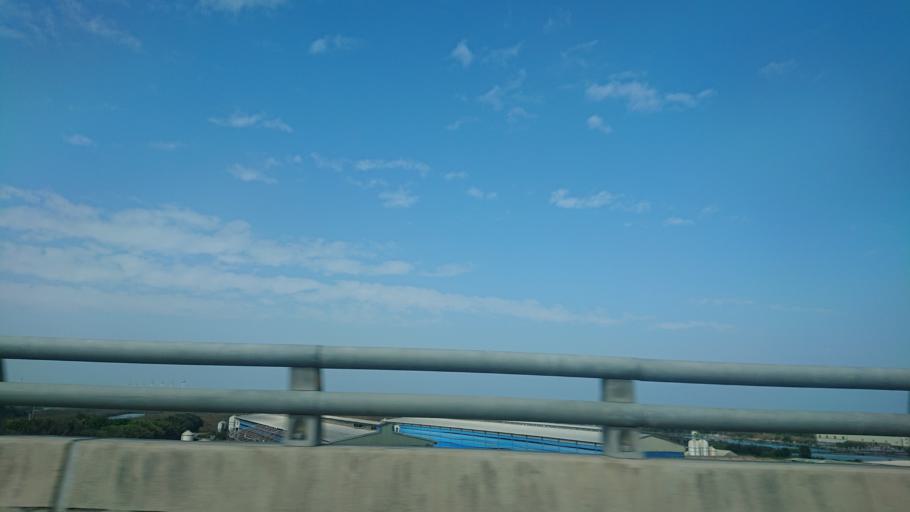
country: TW
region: Taiwan
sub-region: Changhua
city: Chang-hua
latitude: 23.9851
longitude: 120.3672
